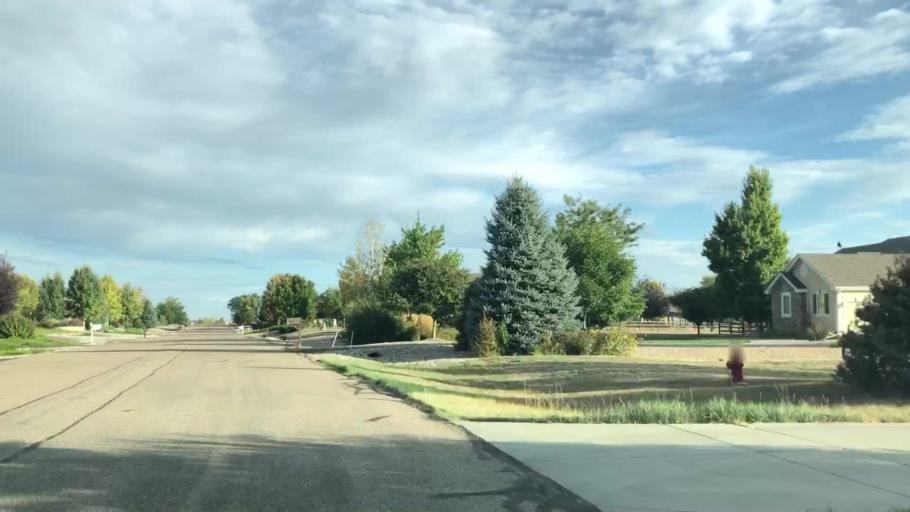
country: US
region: Colorado
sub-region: Weld County
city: Windsor
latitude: 40.4407
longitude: -104.9514
